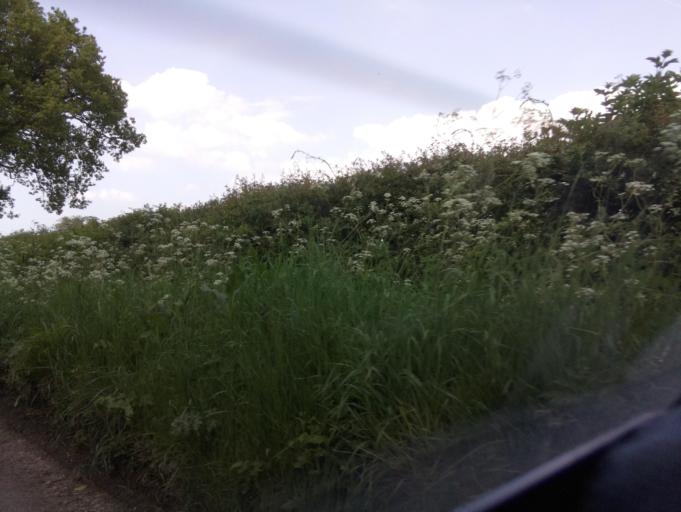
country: GB
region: England
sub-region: Wiltshire
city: Norton
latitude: 51.5533
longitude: -2.1867
